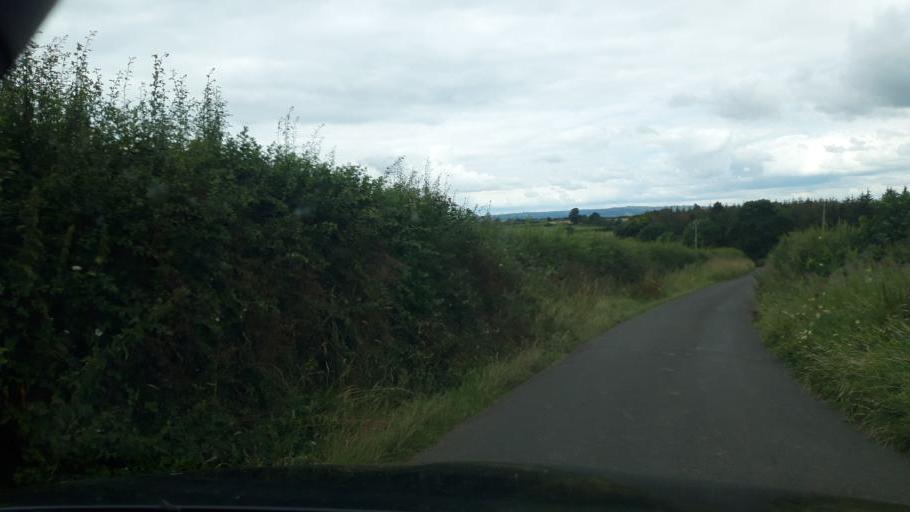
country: IE
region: Leinster
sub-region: Kilkenny
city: Graiguenamanagh
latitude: 52.5926
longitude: -7.0290
